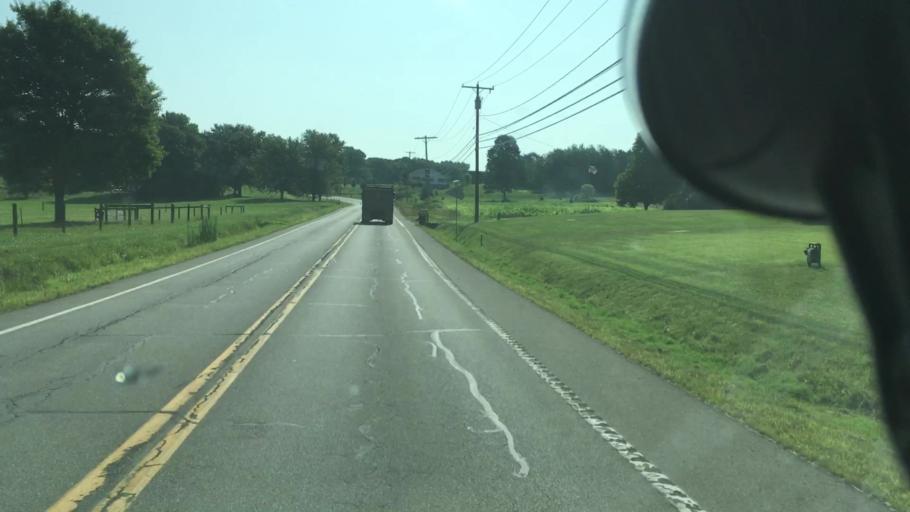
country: US
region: Pennsylvania
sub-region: Lawrence County
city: New Castle
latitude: 41.0139
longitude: -80.2262
